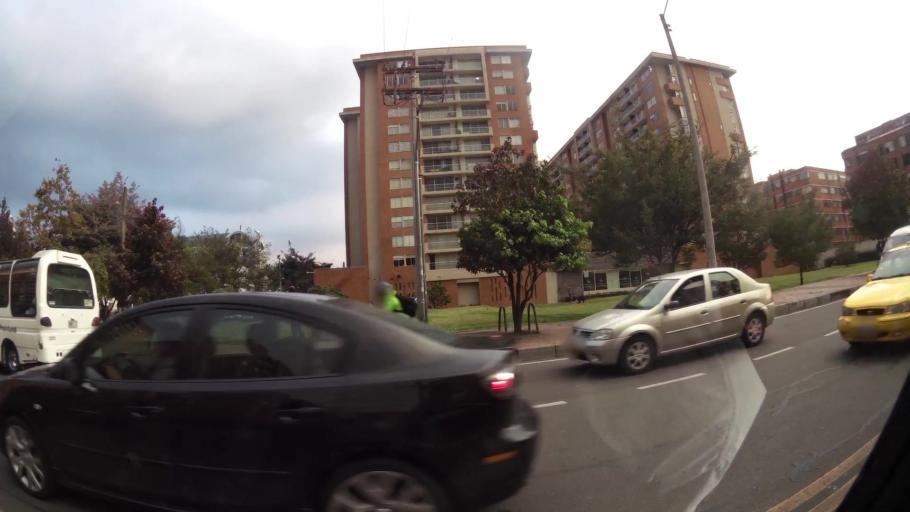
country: CO
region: Bogota D.C.
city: Barrio San Luis
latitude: 4.7286
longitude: -74.0655
